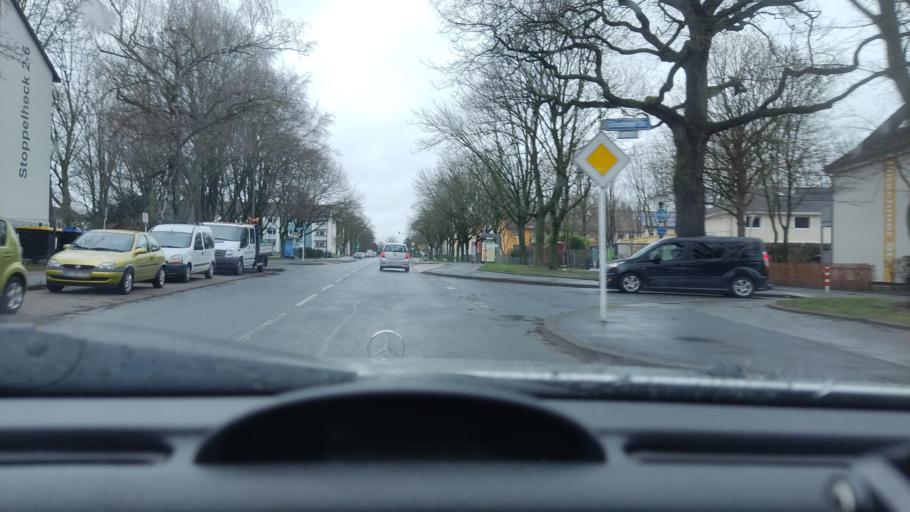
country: DE
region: North Rhine-Westphalia
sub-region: Regierungsbezirk Arnsberg
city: Dortmund
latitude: 51.5552
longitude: 7.4839
